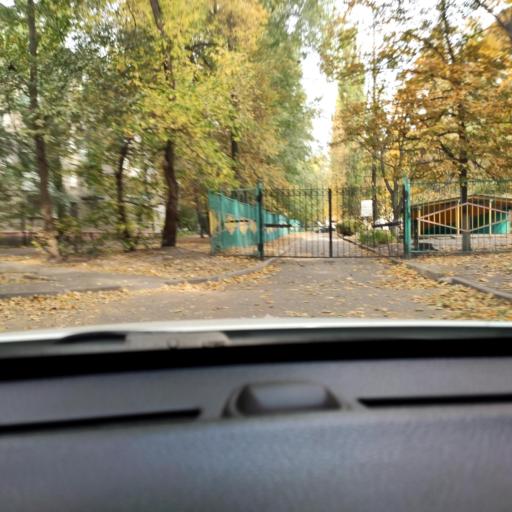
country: RU
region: Voronezj
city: Voronezh
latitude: 51.6990
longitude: 39.1875
